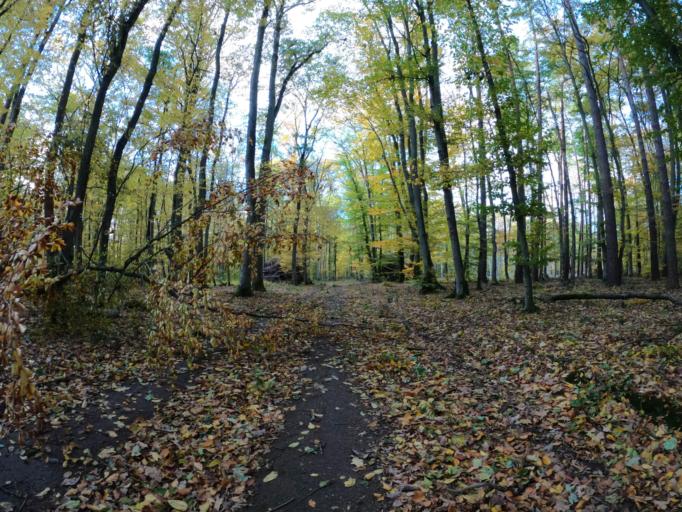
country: PL
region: West Pomeranian Voivodeship
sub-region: Powiat mysliborski
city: Barlinek
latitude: 52.9455
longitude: 15.2766
